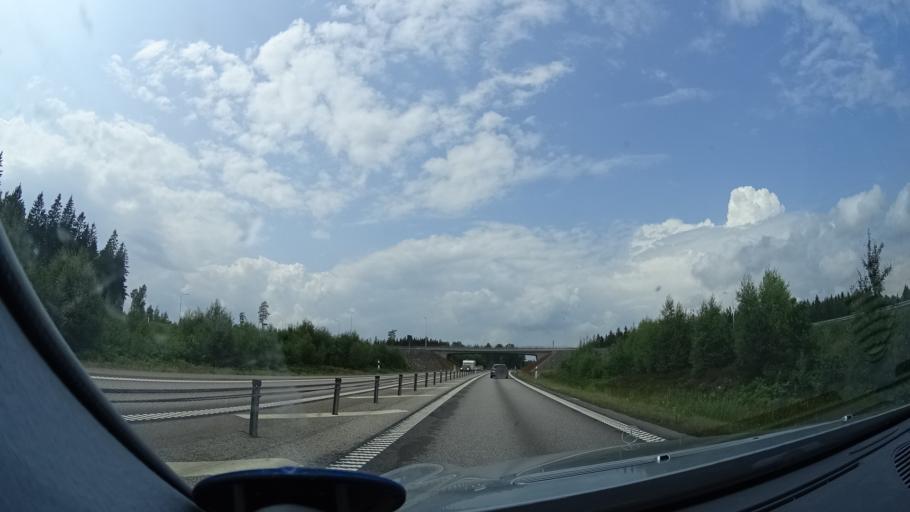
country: SE
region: Kalmar
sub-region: Nybro Kommun
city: Nybro
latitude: 56.7276
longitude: 15.8881
